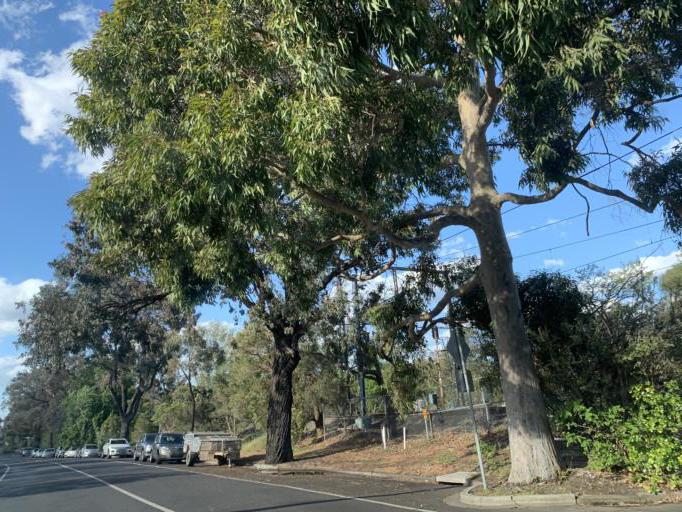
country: AU
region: Victoria
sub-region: Bayside
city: North Brighton
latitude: -37.9094
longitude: 145.0014
